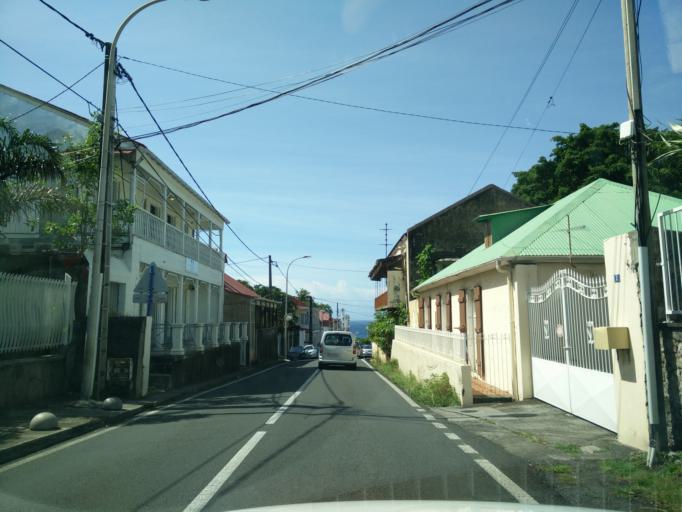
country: GP
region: Guadeloupe
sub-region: Guadeloupe
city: Basse-Terre
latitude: 15.9956
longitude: -61.7246
